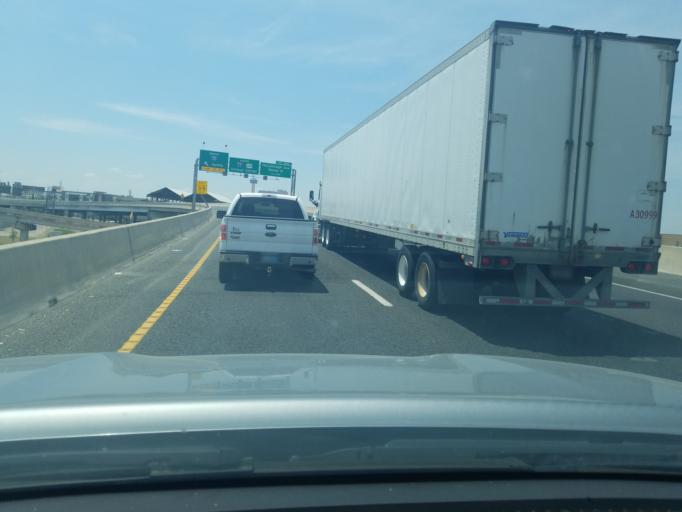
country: US
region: Texas
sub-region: Bexar County
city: San Antonio
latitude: 29.4406
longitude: -98.4791
